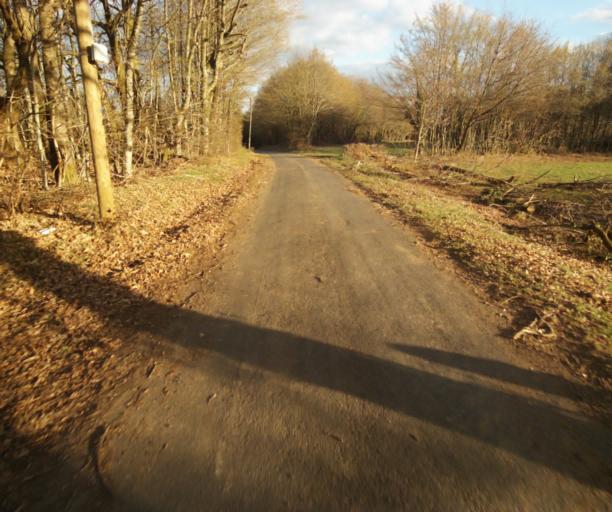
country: FR
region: Limousin
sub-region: Departement de la Correze
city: Uzerche
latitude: 45.3680
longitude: 1.5876
